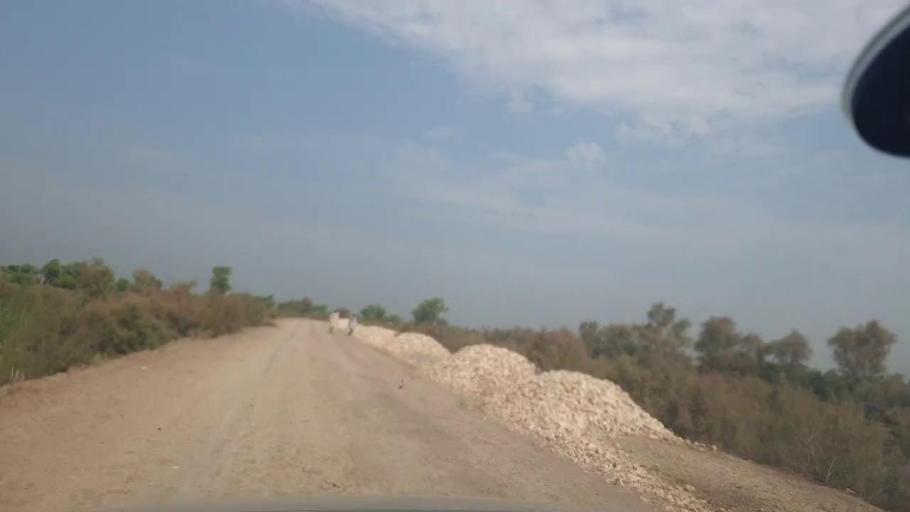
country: PK
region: Balochistan
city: Mehrabpur
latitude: 28.0729
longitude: 68.1002
